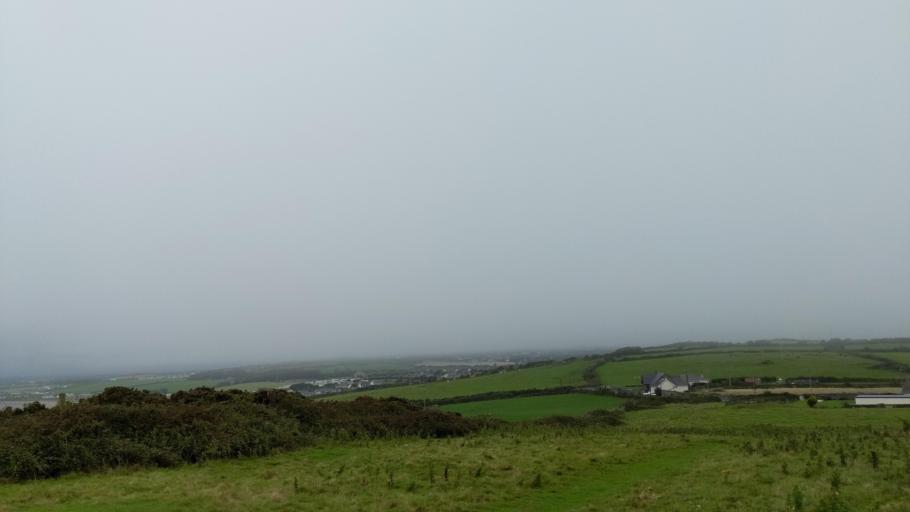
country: IE
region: Leinster
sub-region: Lu
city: Clogherhead
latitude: 53.7945
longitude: -6.2241
